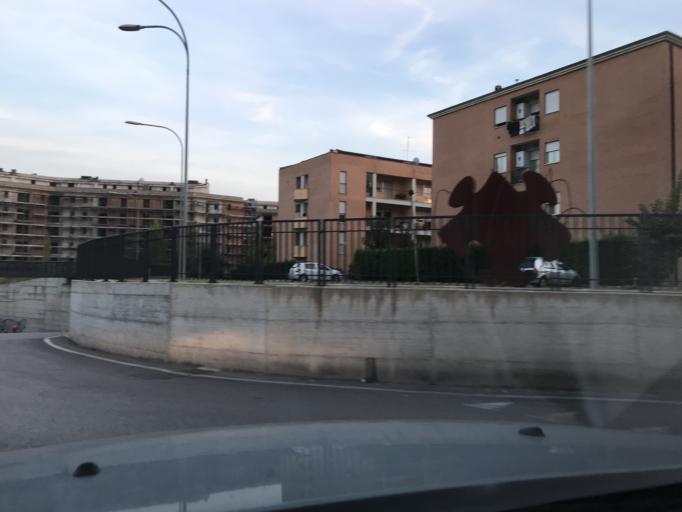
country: IT
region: Umbria
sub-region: Provincia di Perugia
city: Ponte Felcino
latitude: 43.0891
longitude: 12.4293
